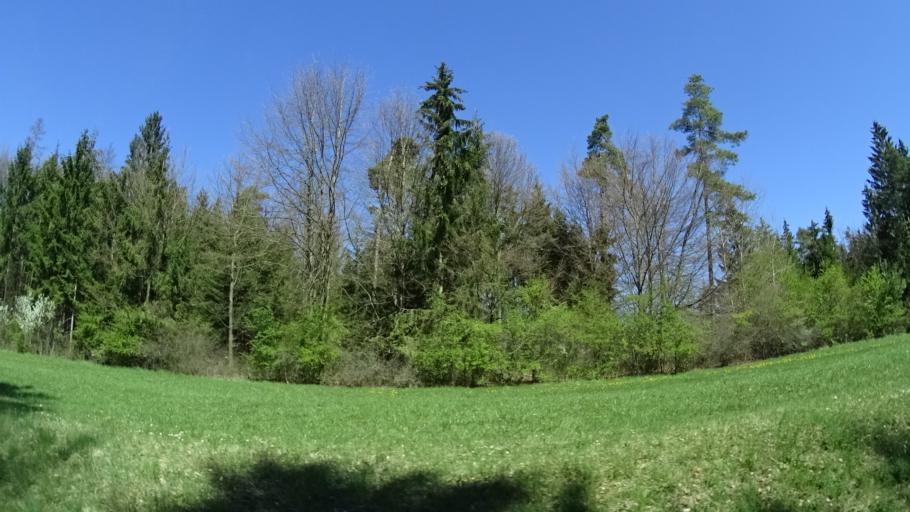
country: DE
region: Bavaria
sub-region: Upper Palatinate
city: Illschwang
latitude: 49.4241
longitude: 11.6800
